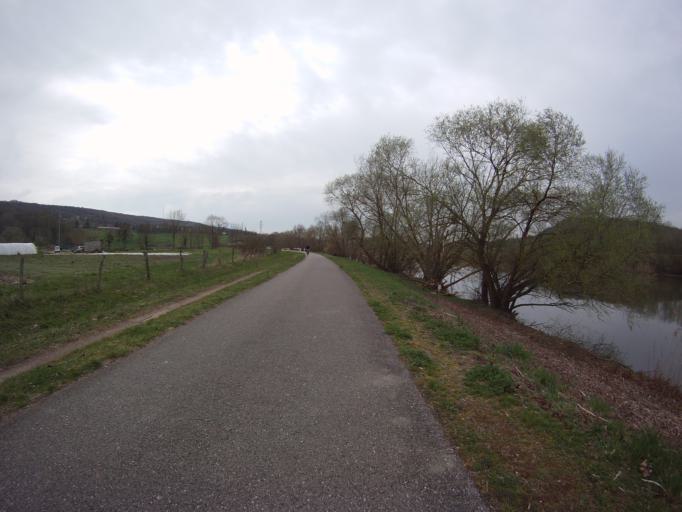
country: FR
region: Lorraine
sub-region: Departement de Meurthe-et-Moselle
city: Champigneulles
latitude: 48.7335
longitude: 6.1726
